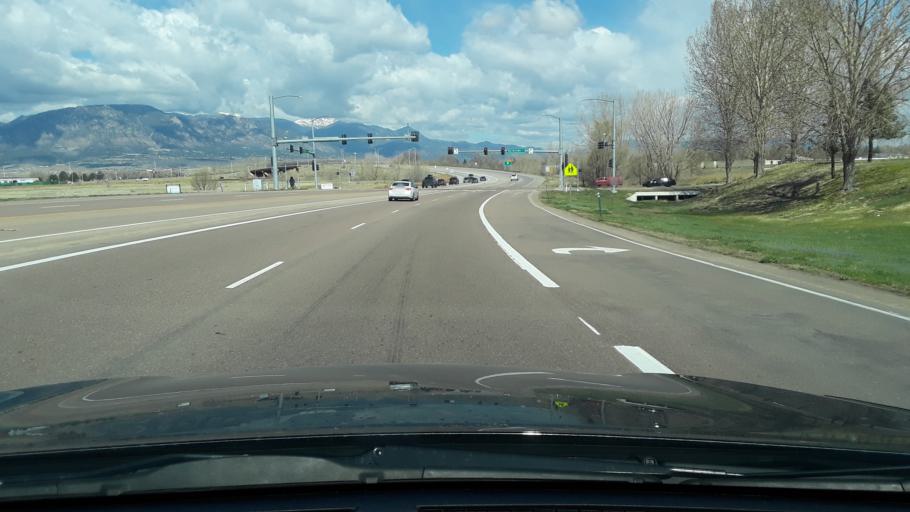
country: US
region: Colorado
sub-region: El Paso County
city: Security-Widefield
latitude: 38.7207
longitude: -104.7108
